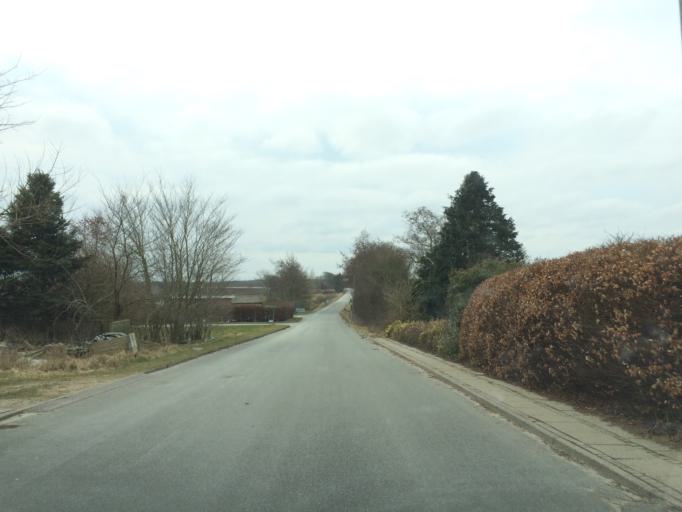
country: DK
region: South Denmark
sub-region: Varde Kommune
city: Oksbol
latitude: 55.7951
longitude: 8.3602
